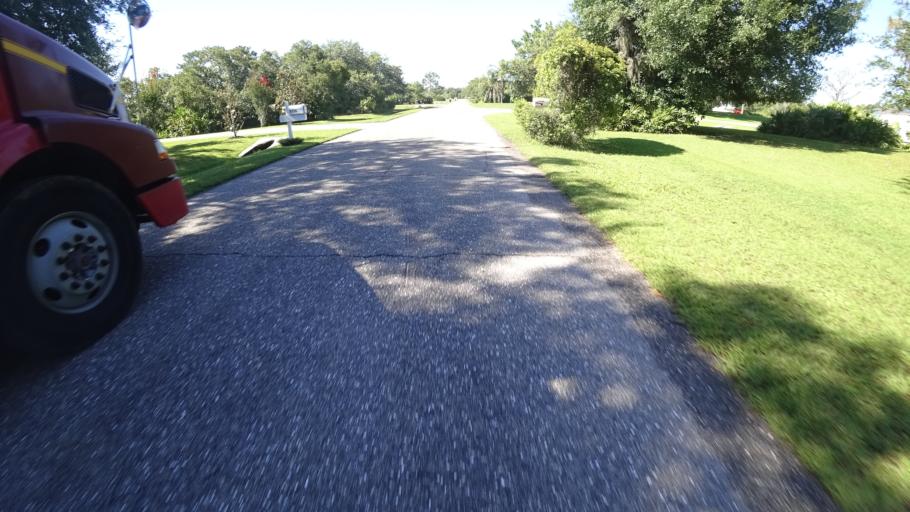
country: US
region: Florida
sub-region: Sarasota County
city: Fruitville
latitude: 27.4003
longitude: -82.3013
